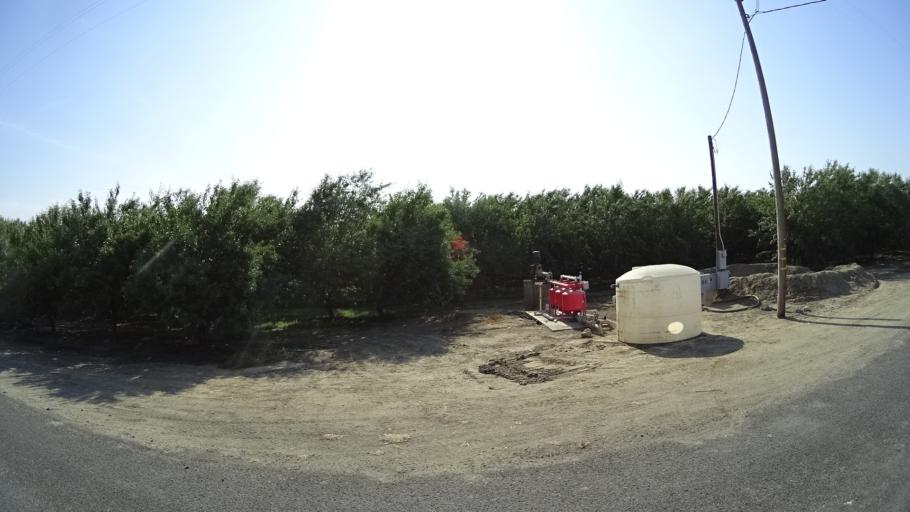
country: US
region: California
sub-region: Fresno County
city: Riverdale
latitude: 36.3794
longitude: -119.8162
